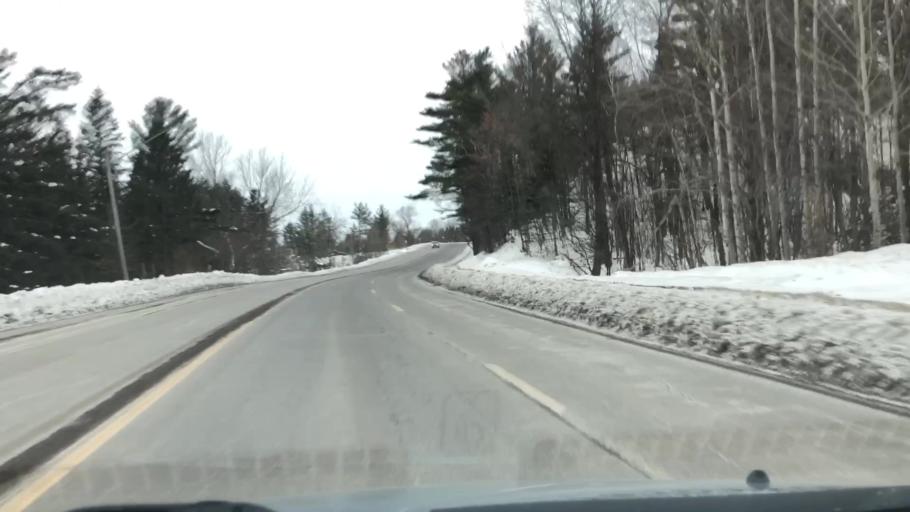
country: US
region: Minnesota
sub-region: Saint Louis County
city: Arnold
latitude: 46.8389
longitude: -92.0799
